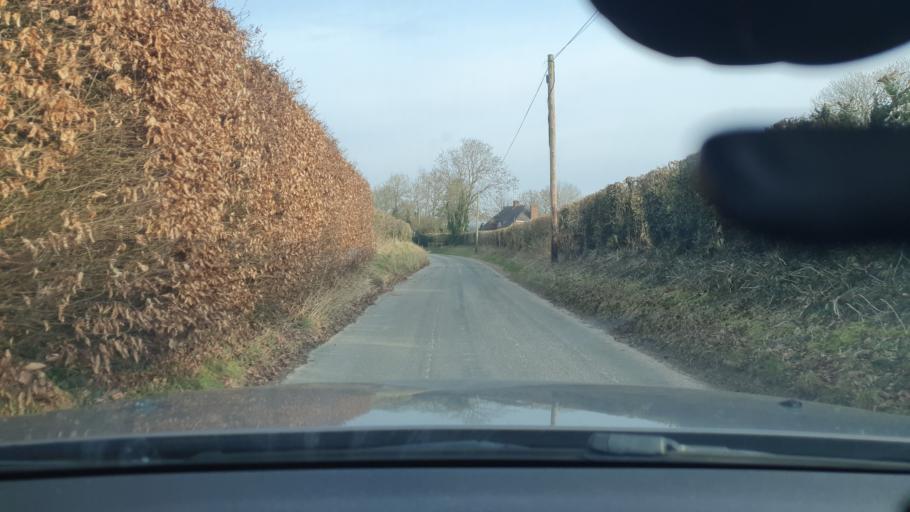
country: GB
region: England
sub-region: Wiltshire
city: Shalbourne
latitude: 51.3539
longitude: -1.5449
